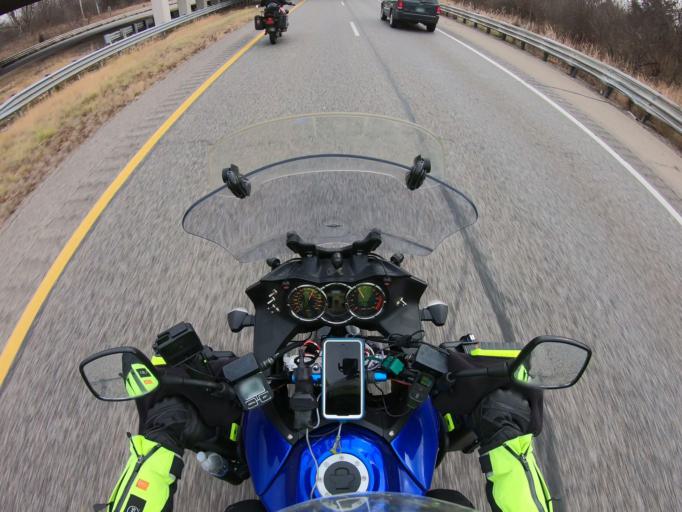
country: US
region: Michigan
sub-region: Genesee County
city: Grand Blanc
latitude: 42.9296
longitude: -83.6907
